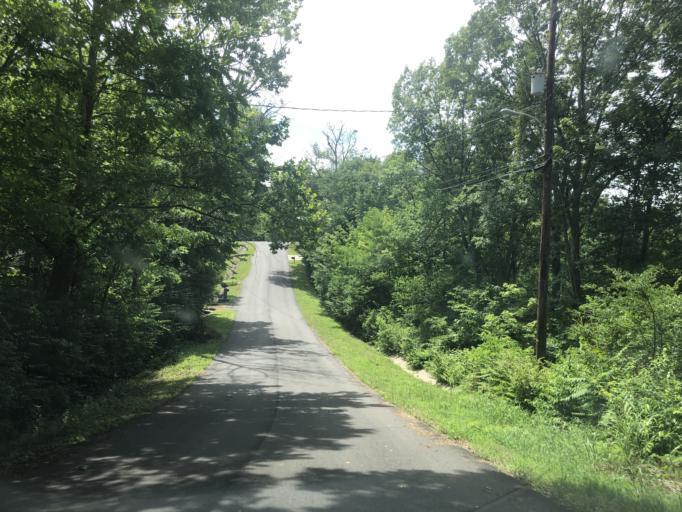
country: US
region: Tennessee
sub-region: Davidson County
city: Belle Meade
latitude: 36.0800
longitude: -86.9308
